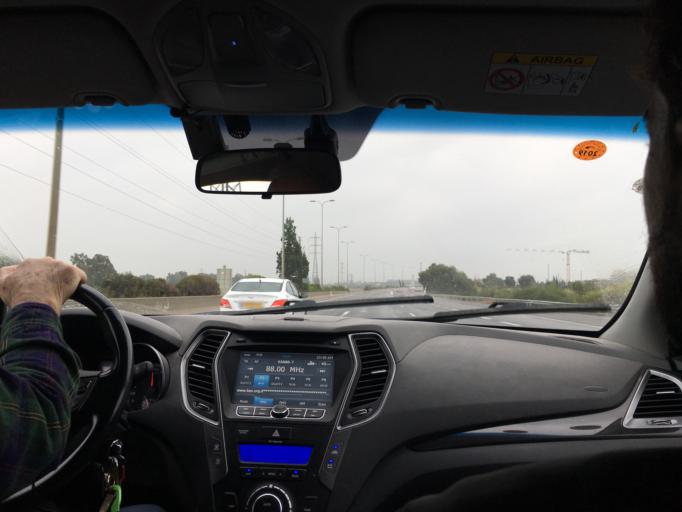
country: IL
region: Tel Aviv
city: Ramat HaSharon
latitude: 32.1210
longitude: 34.8648
